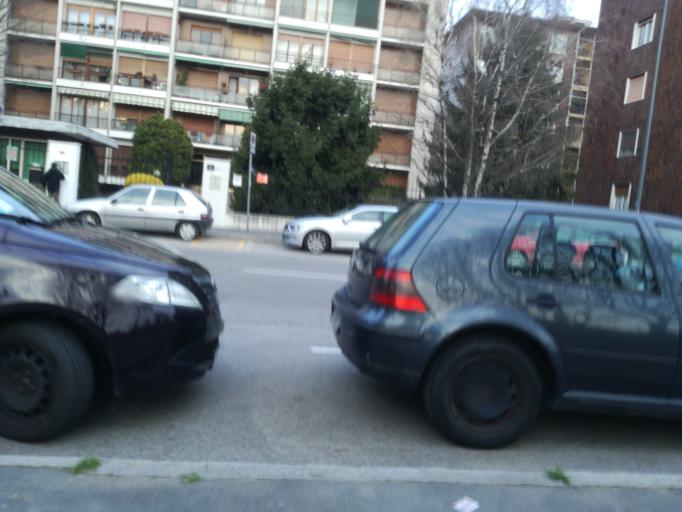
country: IT
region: Lombardy
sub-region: Citta metropolitana di Milano
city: Romano Banco
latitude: 45.4568
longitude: 9.1271
